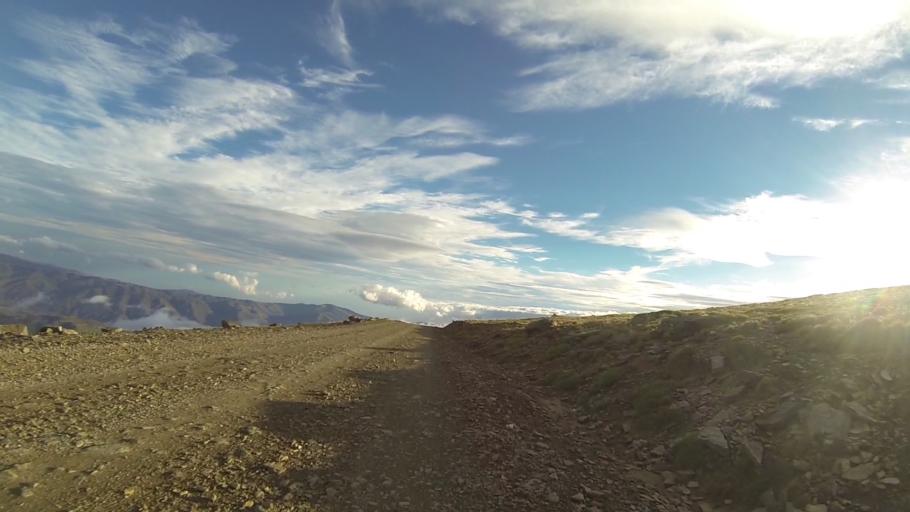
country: ES
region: Andalusia
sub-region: Provincia de Granada
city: Portugos
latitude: 36.9869
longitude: -3.3140
